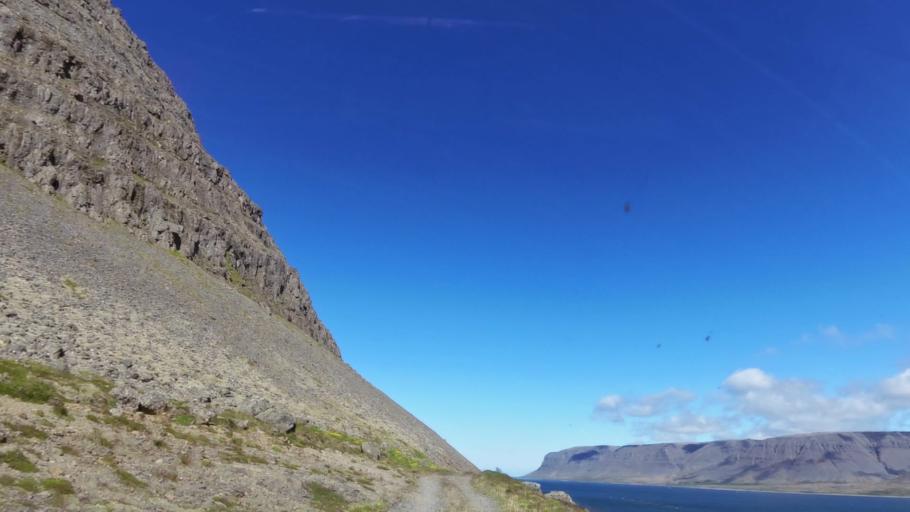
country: IS
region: West
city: Olafsvik
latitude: 65.6264
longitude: -23.9003
